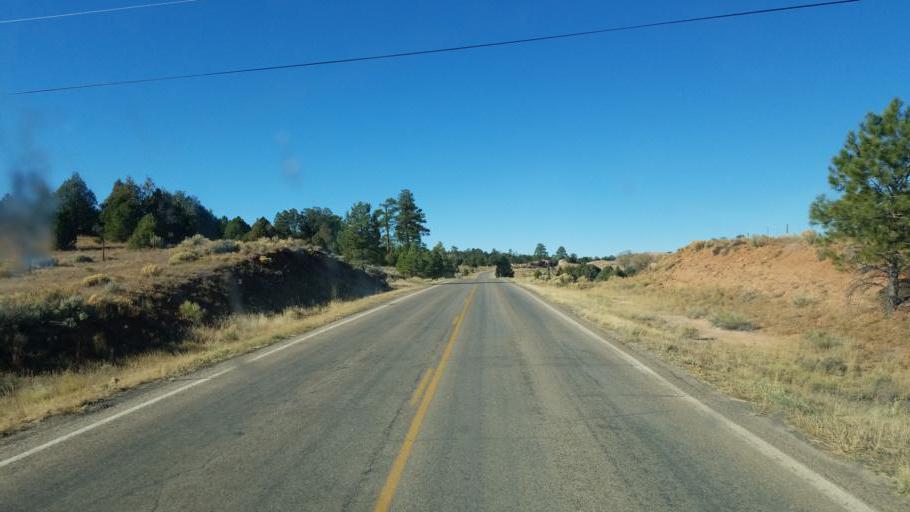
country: US
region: New Mexico
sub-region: McKinley County
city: Navajo
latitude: 36.0415
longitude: -108.9625
